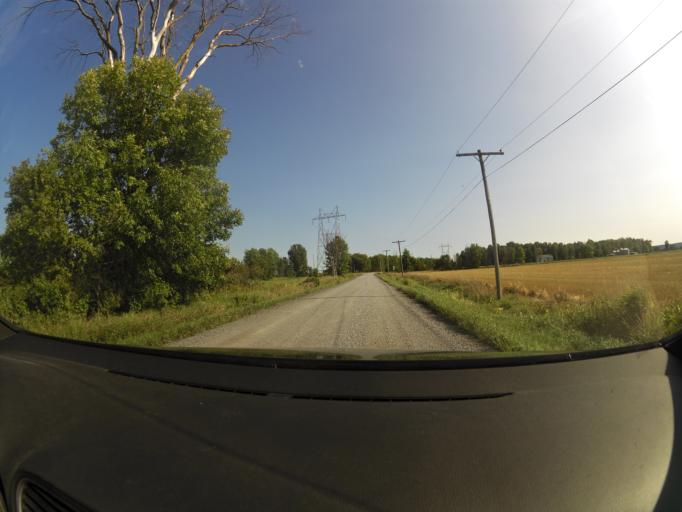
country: CA
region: Ontario
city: Arnprior
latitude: 45.3844
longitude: -76.3230
